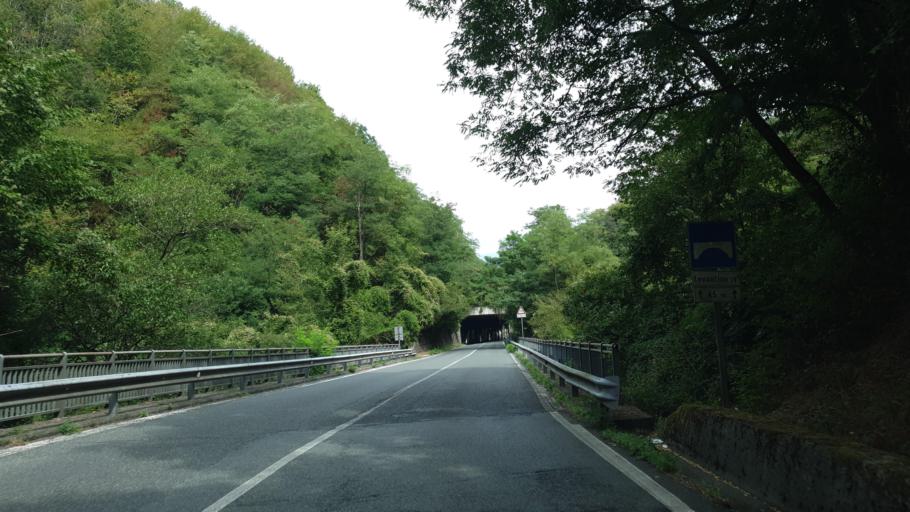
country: IT
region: Liguria
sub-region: Provincia di La Spezia
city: Carrodano
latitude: 44.2192
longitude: 9.6283
